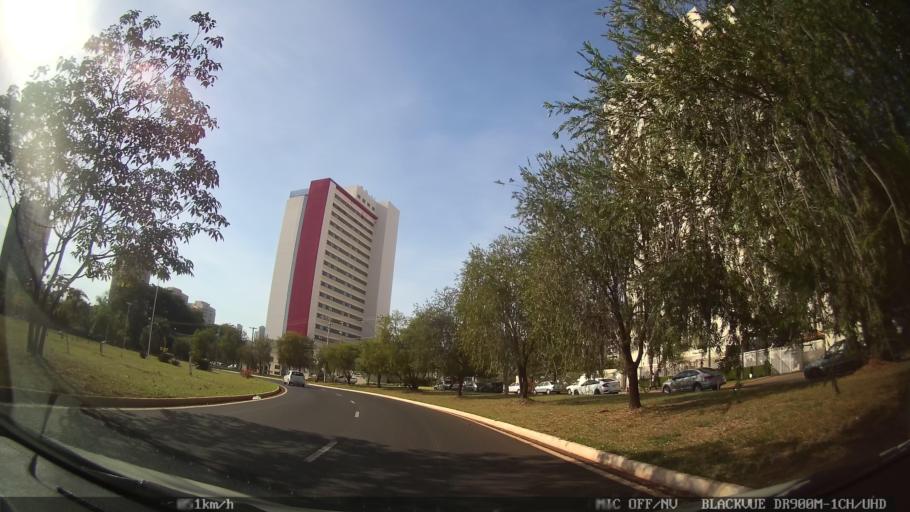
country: BR
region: Sao Paulo
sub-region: Ribeirao Preto
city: Ribeirao Preto
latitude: -21.2164
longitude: -47.8226
